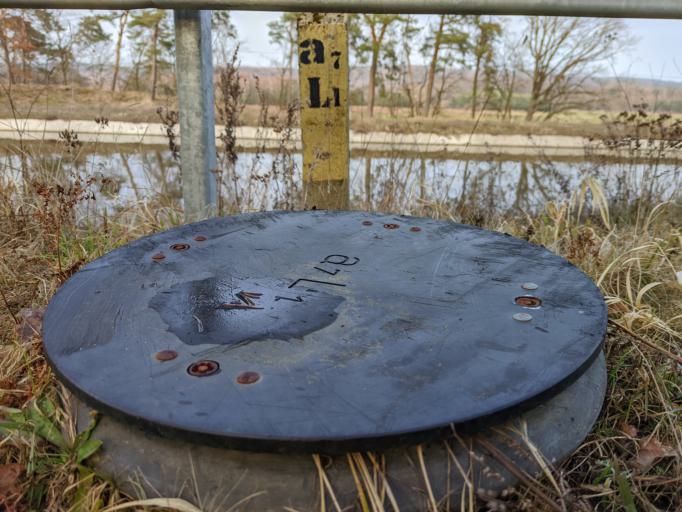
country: PL
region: Lubusz
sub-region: Powiat zielonogorski
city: Nowogrod Bobrzanski
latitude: 51.8407
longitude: 15.1973
